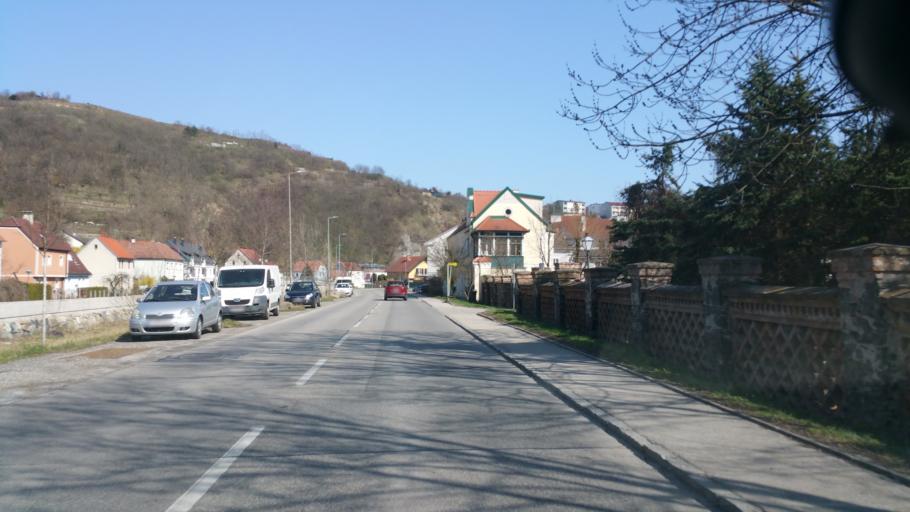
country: AT
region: Lower Austria
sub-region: Krems an der Donau Stadt
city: Krems an der Donau
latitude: 48.4209
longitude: 15.5970
